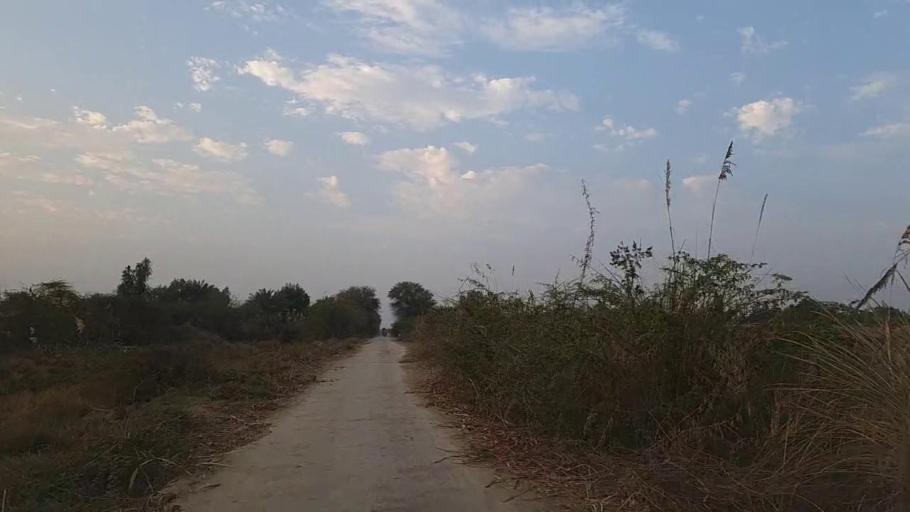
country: PK
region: Sindh
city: Mirwah Gorchani
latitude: 25.3408
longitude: 69.2071
